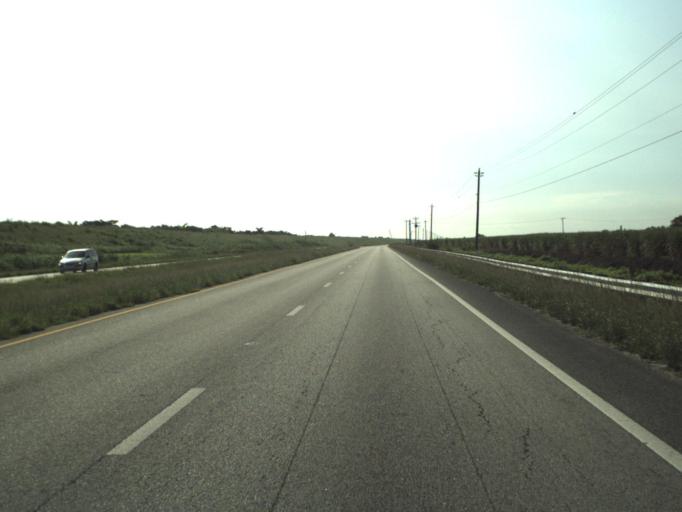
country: US
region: Florida
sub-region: Palm Beach County
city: South Bay
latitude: 26.6958
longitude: -80.7770
